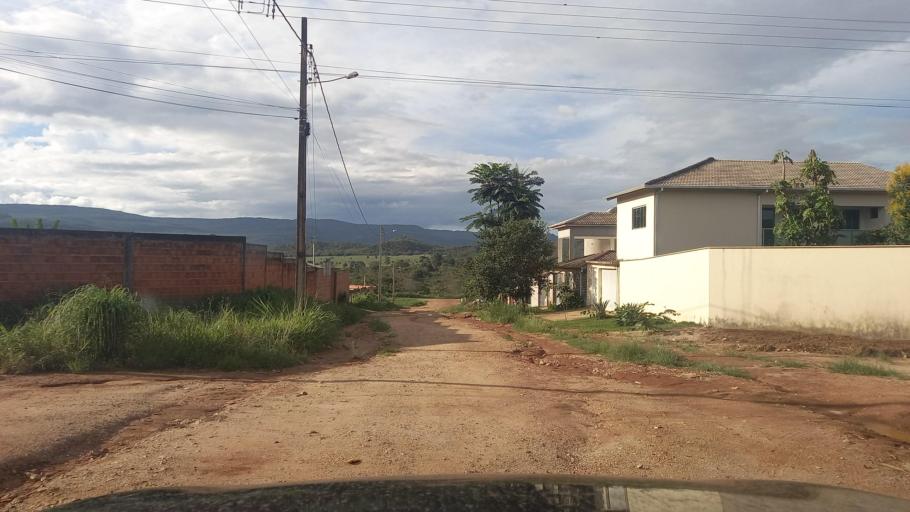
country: BR
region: Goias
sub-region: Cavalcante
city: Cavalcante
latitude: -13.7942
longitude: -47.4427
